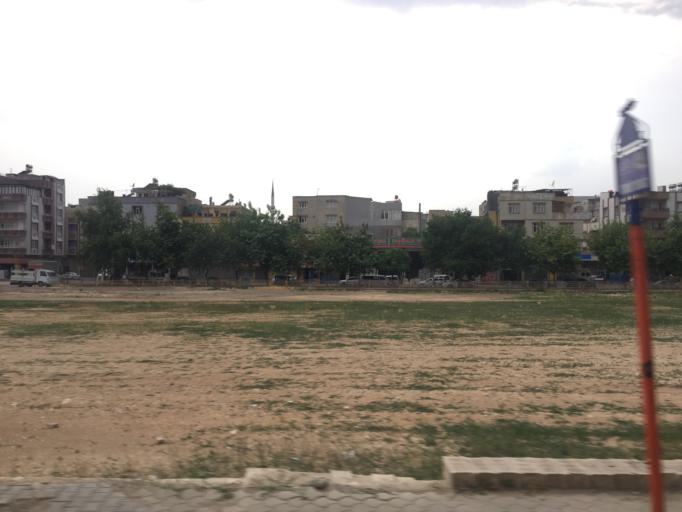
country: TR
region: Gaziantep
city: Gaziantep
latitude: 37.0661
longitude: 37.4146
